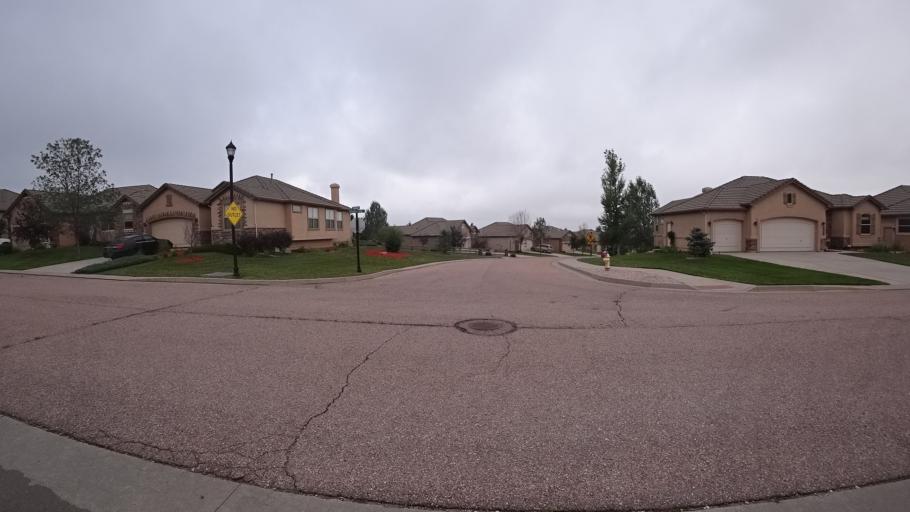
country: US
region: Colorado
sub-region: El Paso County
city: Gleneagle
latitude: 39.0338
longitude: -104.7775
